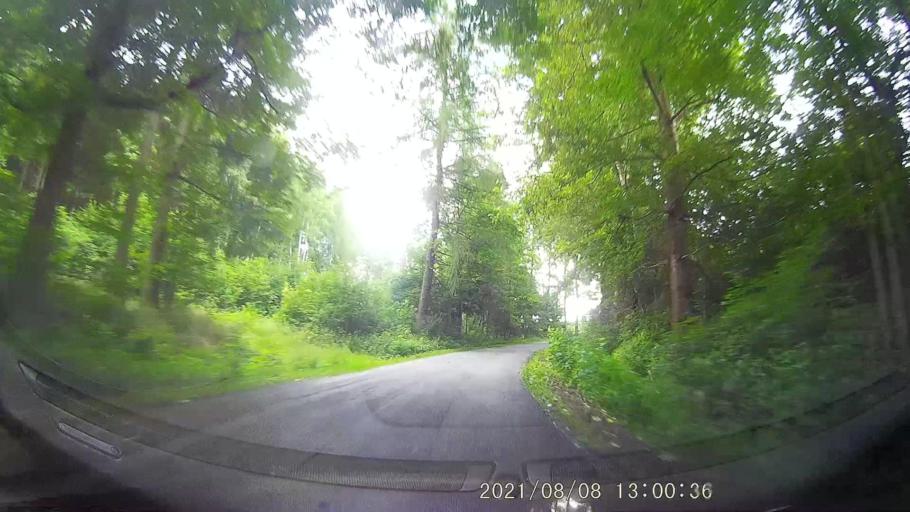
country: PL
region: Lower Silesian Voivodeship
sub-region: Powiat klodzki
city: Duszniki-Zdroj
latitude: 50.4149
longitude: 16.3428
